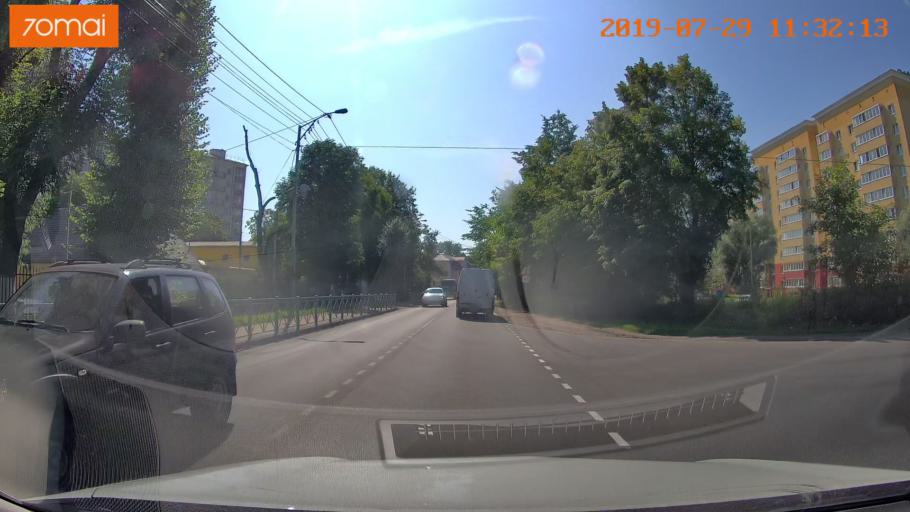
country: RU
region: Kaliningrad
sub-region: Gorod Kaliningrad
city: Kaliningrad
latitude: 54.6721
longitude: 20.5445
